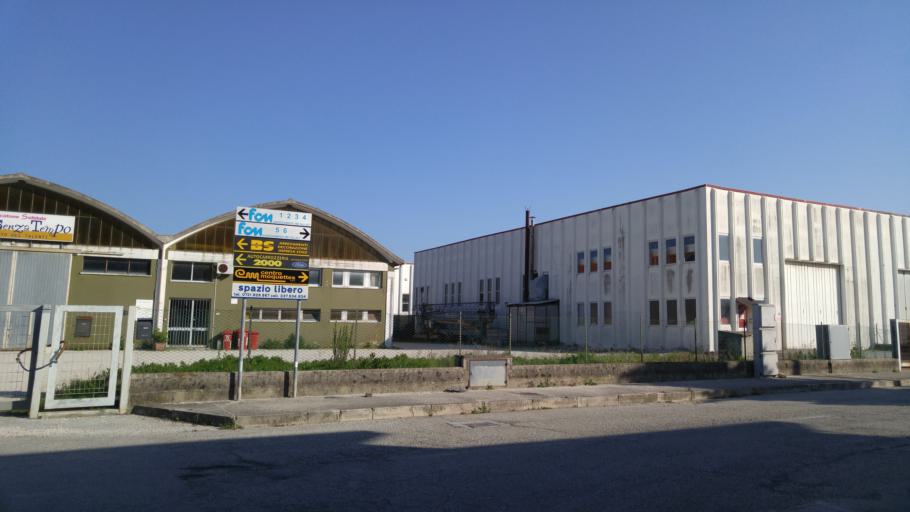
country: IT
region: The Marches
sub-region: Provincia di Pesaro e Urbino
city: Rosciano
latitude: 43.8048
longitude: 12.9801
